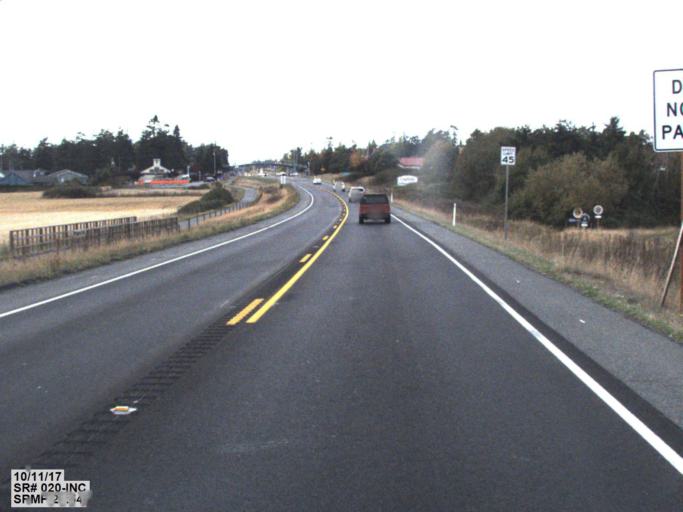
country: US
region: Washington
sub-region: Island County
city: Coupeville
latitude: 48.2122
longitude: -122.6800
